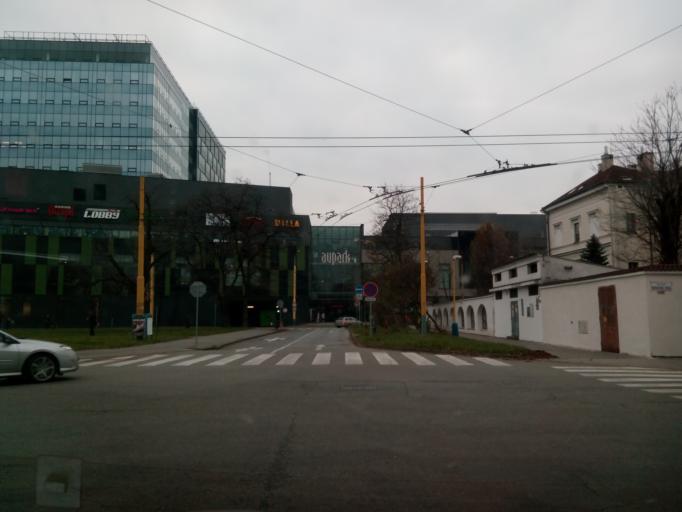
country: SK
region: Kosicky
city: Kosice
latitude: 48.7192
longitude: 21.2631
